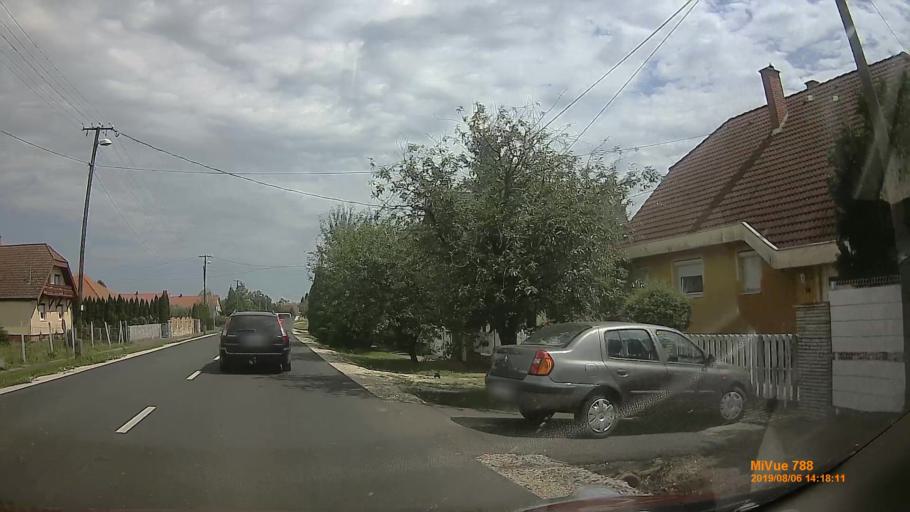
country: HU
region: Vas
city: Taplanszentkereszt
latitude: 47.1849
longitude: 16.7406
